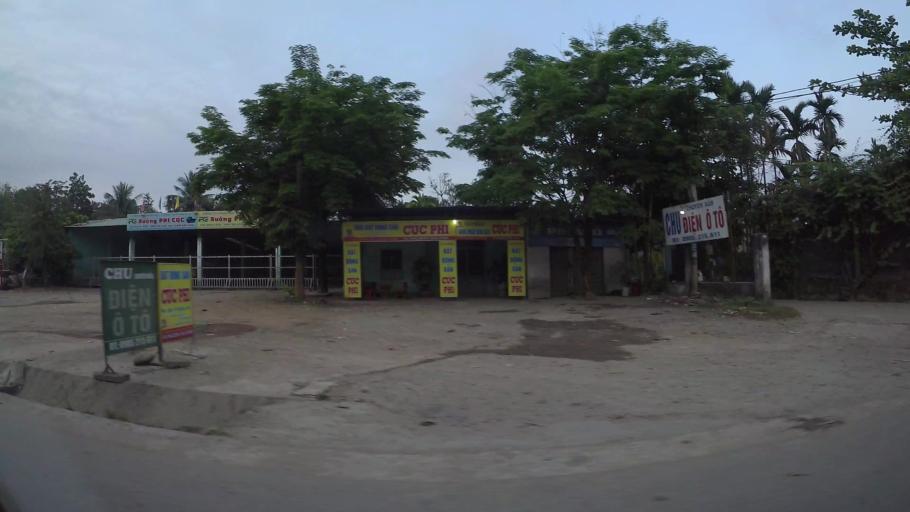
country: VN
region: Da Nang
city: Lien Chieu
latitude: 16.0548
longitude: 108.1021
